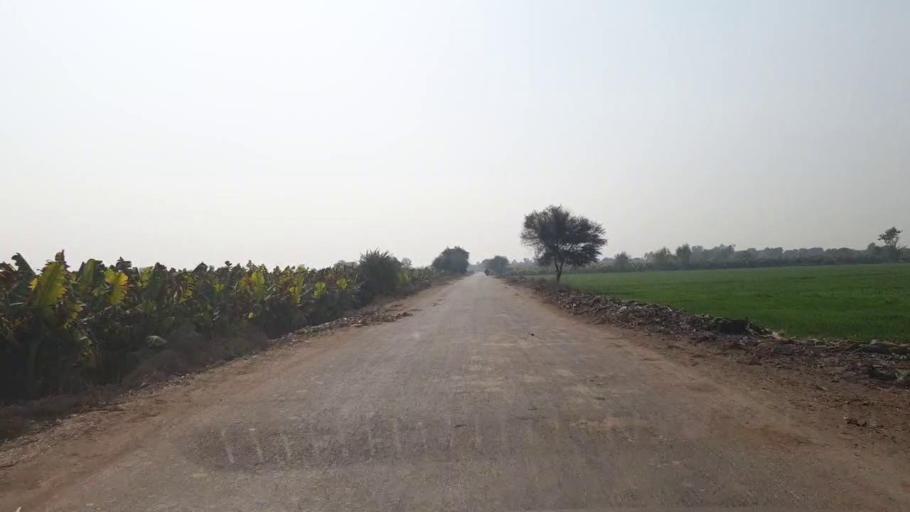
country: PK
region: Sindh
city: Hala
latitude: 25.8681
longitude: 68.4302
